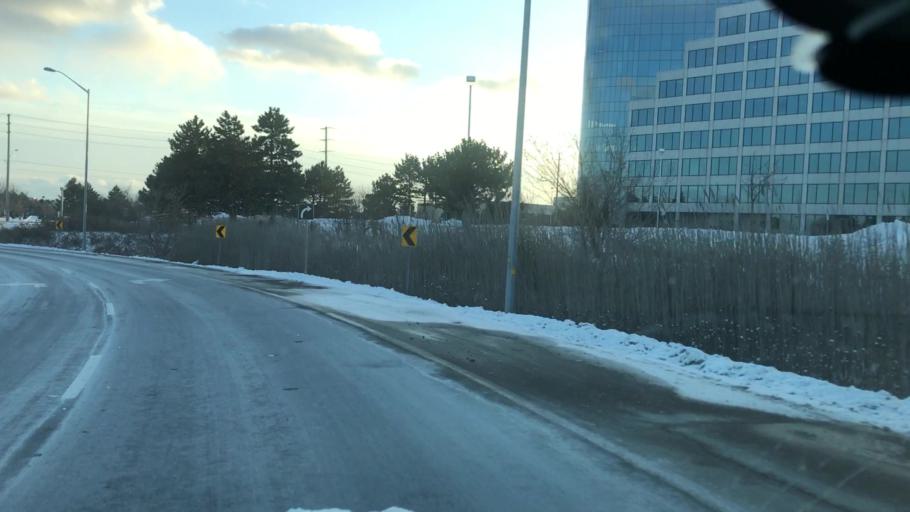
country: CA
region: Ontario
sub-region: York
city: Richmond Hill
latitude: 43.8658
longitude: -79.3776
